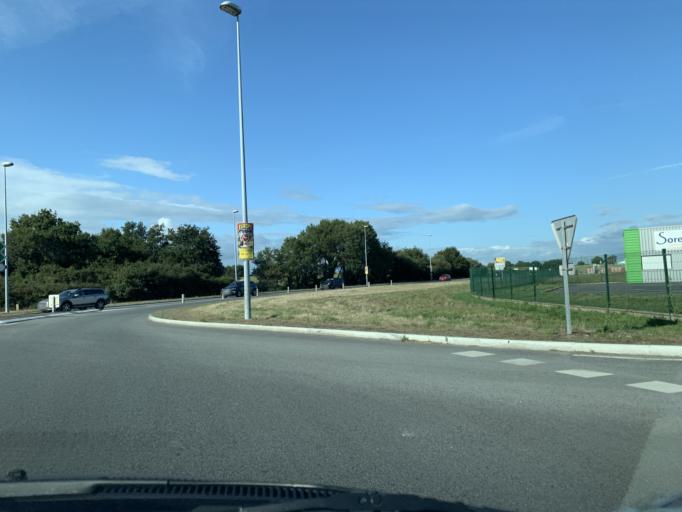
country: FR
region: Brittany
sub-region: Departement du Morbihan
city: Nivillac
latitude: 47.5054
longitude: -2.3004
